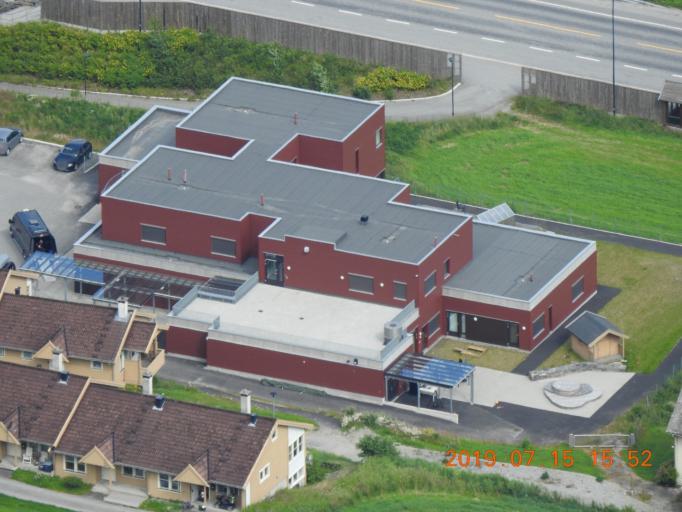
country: NO
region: Hordaland
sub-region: Voss
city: Voss
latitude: 60.6455
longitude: 6.4080
